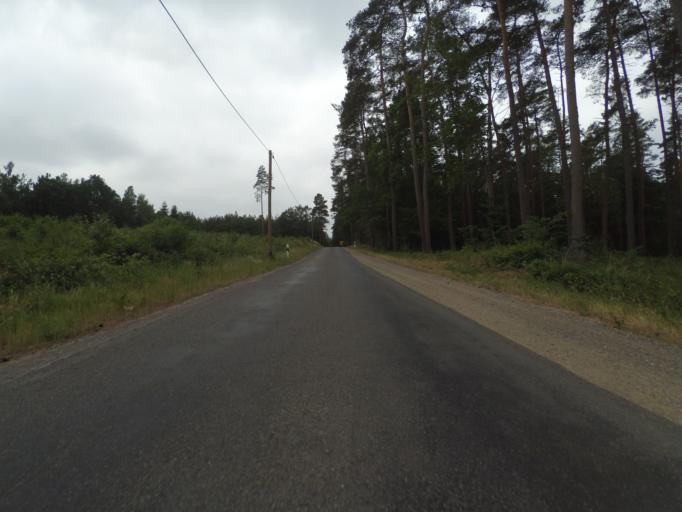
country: DE
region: Mecklenburg-Vorpommern
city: Domsuhl
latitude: 53.4914
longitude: 11.7975
